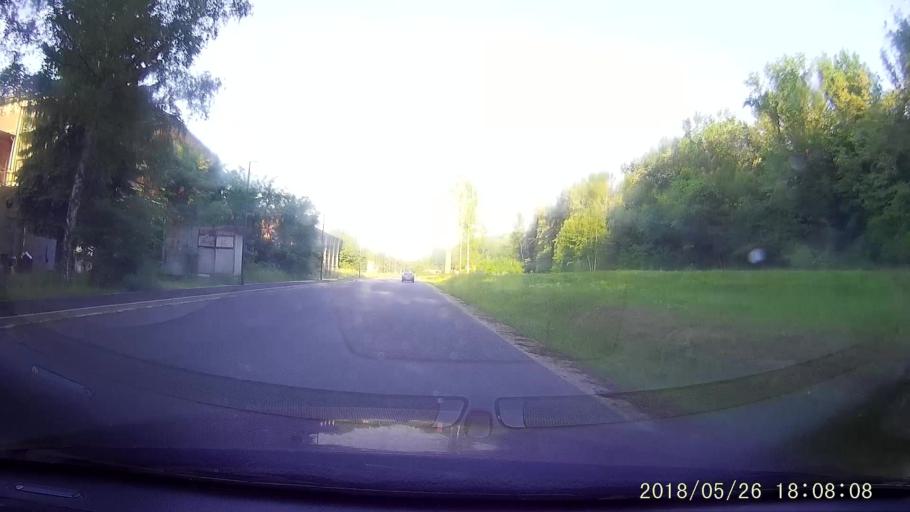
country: DE
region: Saxony
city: Schonau-Berzdorf
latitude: 51.0677
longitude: 14.9327
